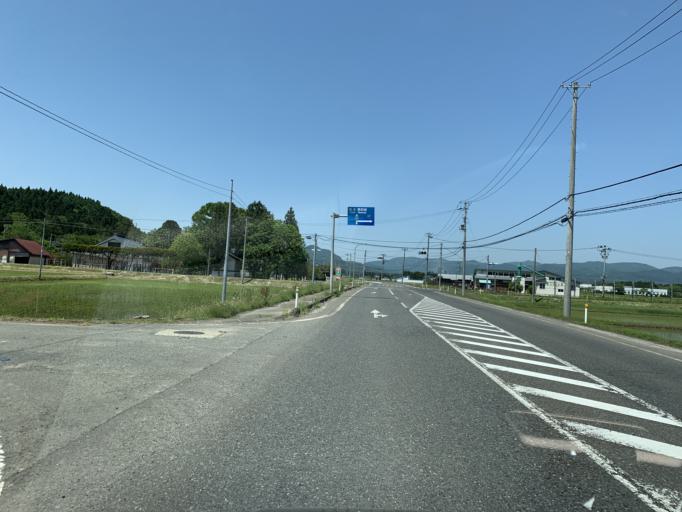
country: JP
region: Iwate
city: Kitakami
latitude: 39.2834
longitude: 141.0332
